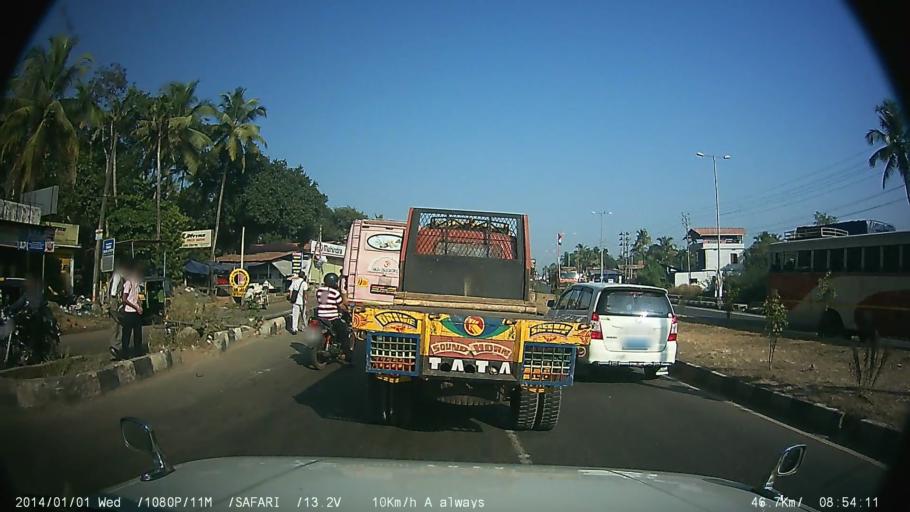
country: IN
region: Kerala
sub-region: Ernakulam
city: Angamali
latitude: 10.2167
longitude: 76.3778
